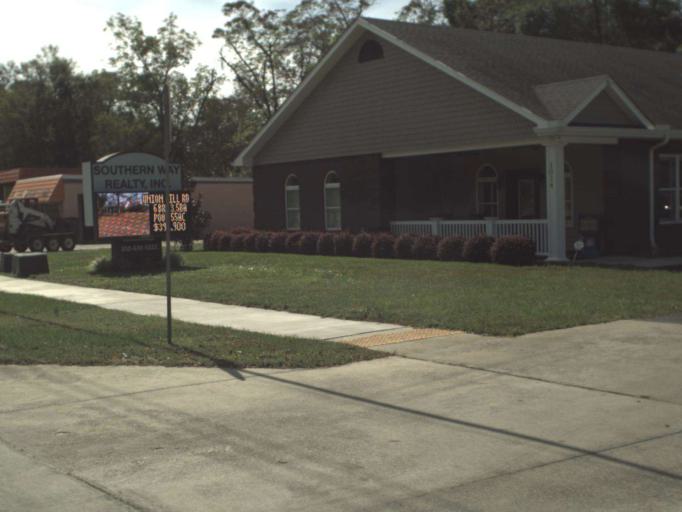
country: US
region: Florida
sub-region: Washington County
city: Chipley
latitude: 30.7731
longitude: -85.5377
